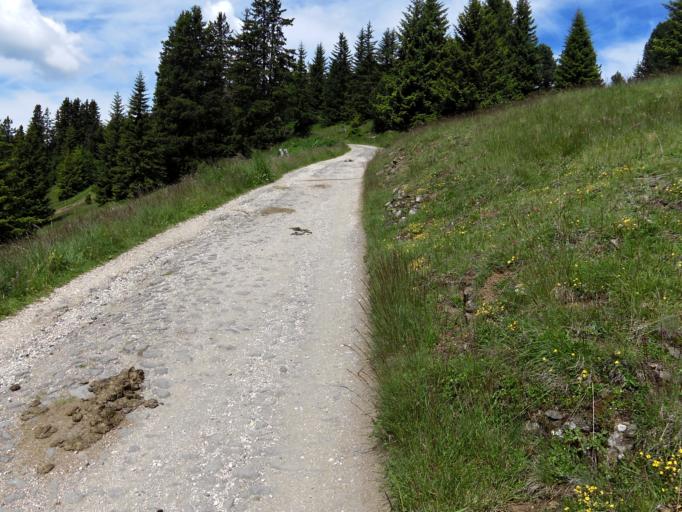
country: IT
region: Trentino-Alto Adige
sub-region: Bolzano
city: Ortisei
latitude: 46.5577
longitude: 11.6684
